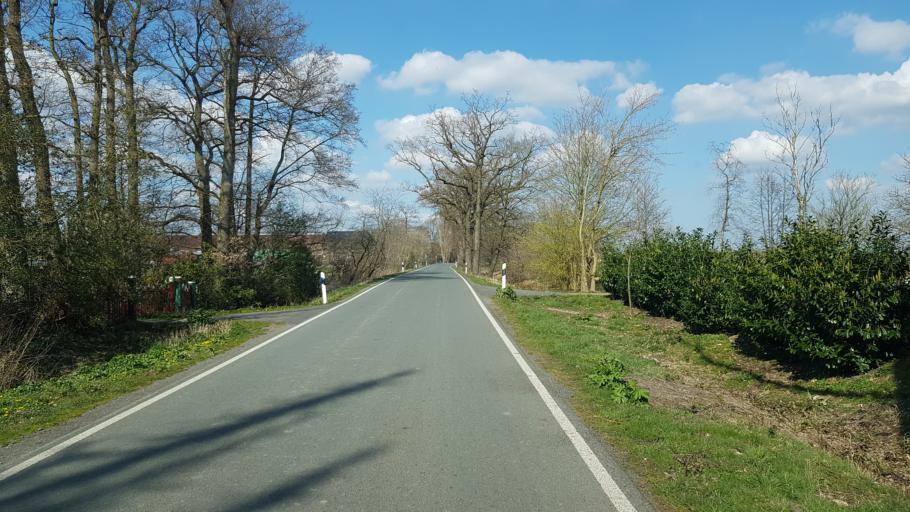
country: DE
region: Lower Saxony
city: Rastede
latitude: 53.3214
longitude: 8.2289
